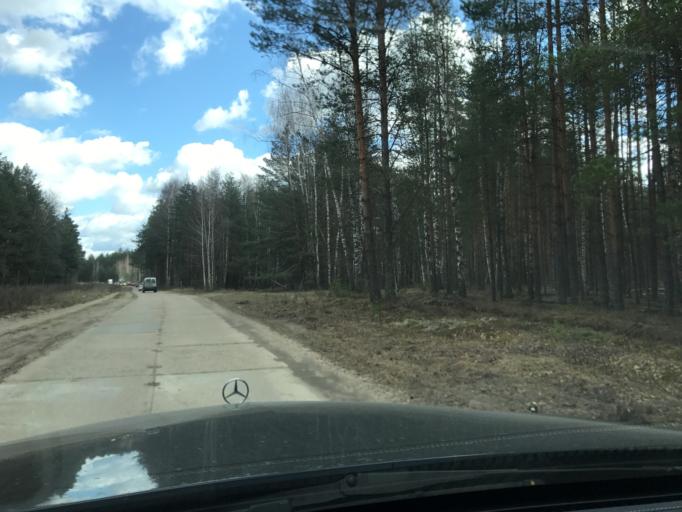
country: RU
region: Vladimir
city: Pokrov
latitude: 55.8648
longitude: 39.2228
